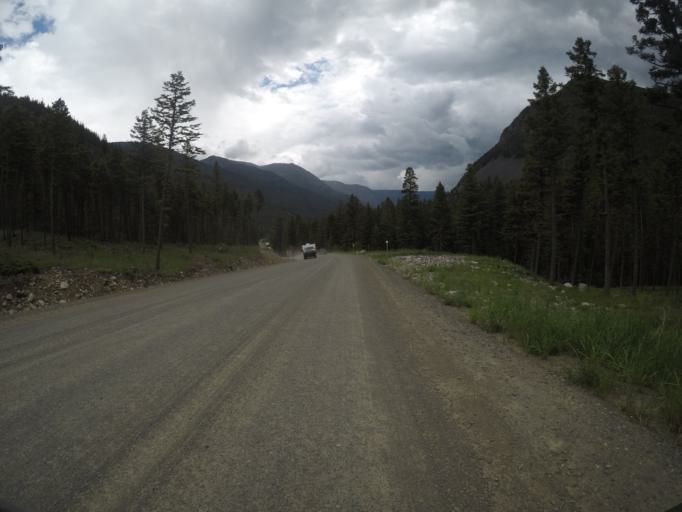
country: US
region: Montana
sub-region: Park County
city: Livingston
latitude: 45.4765
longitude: -110.2059
